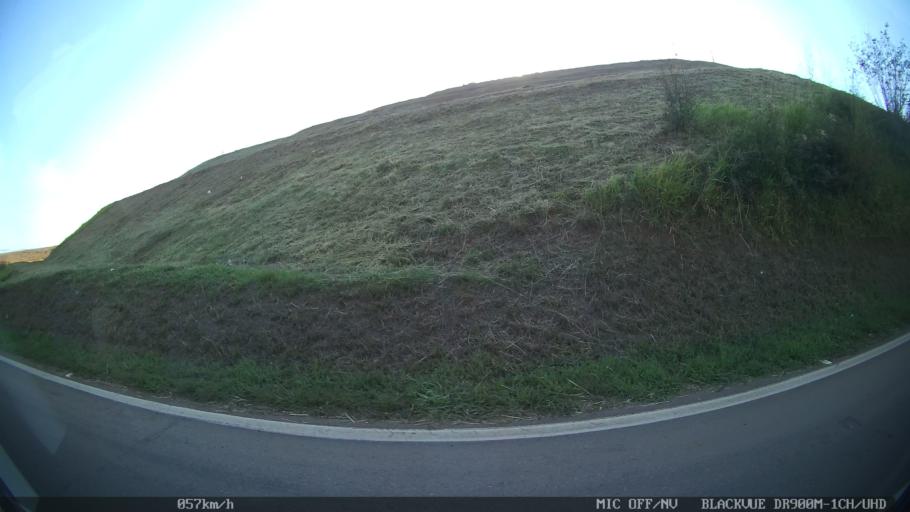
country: BR
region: Sao Paulo
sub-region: Piracicaba
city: Piracicaba
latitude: -22.6894
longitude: -47.5992
